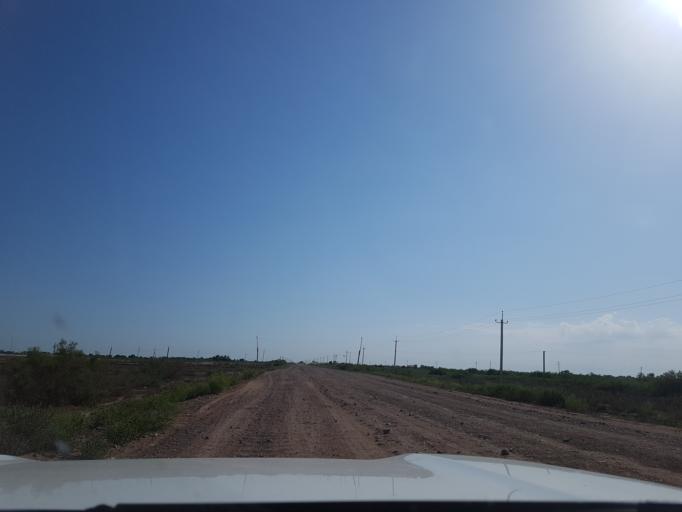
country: TM
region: Dasoguz
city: Koeneuergench
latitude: 42.0615
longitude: 58.8462
